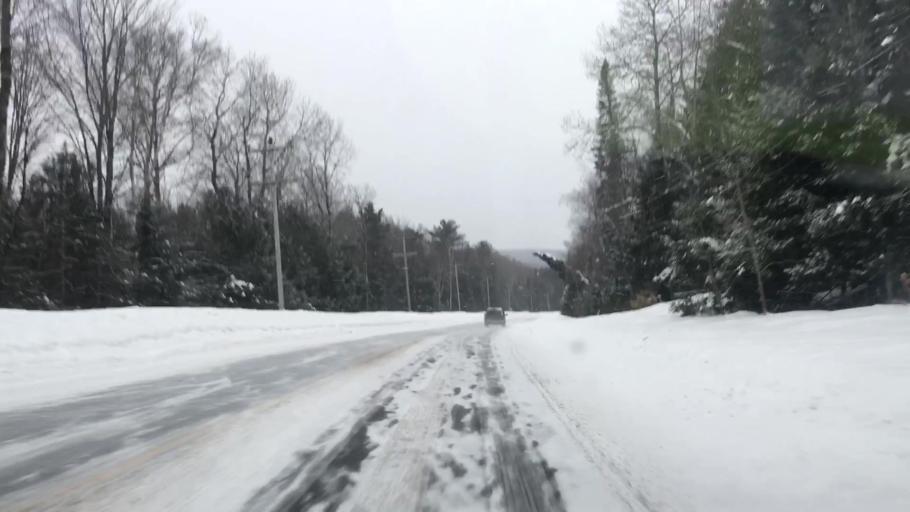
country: US
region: Maine
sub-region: Penobscot County
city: Medway
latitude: 45.5967
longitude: -68.4764
